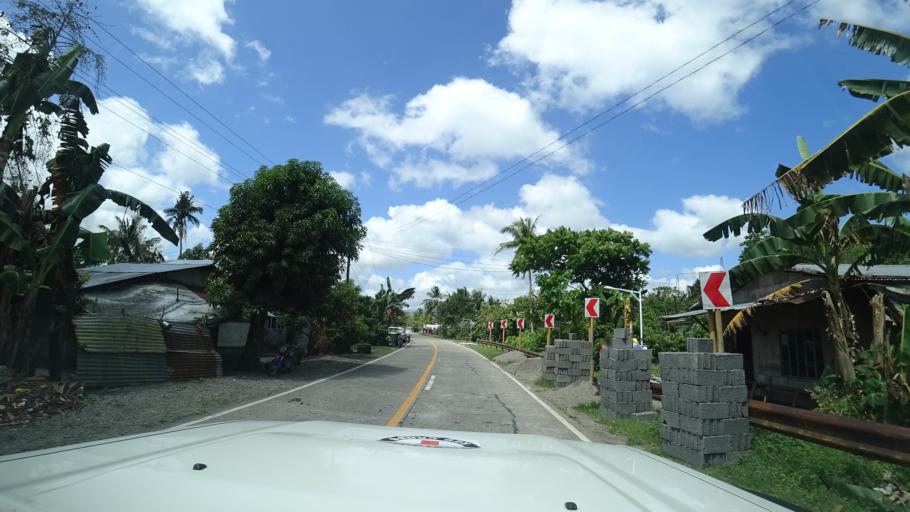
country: PH
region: Eastern Visayas
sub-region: Province of Leyte
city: Mayorga
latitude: 10.9053
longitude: 124.9955
